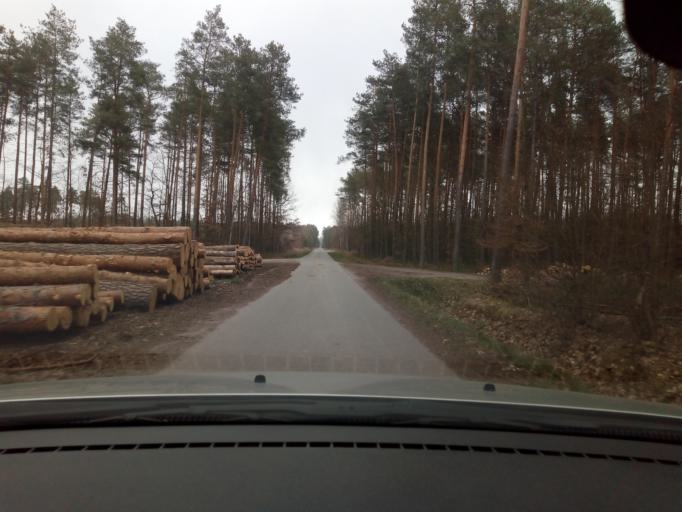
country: PL
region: Swietokrzyskie
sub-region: Powiat starachowicki
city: Brody
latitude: 51.0744
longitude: 21.3226
